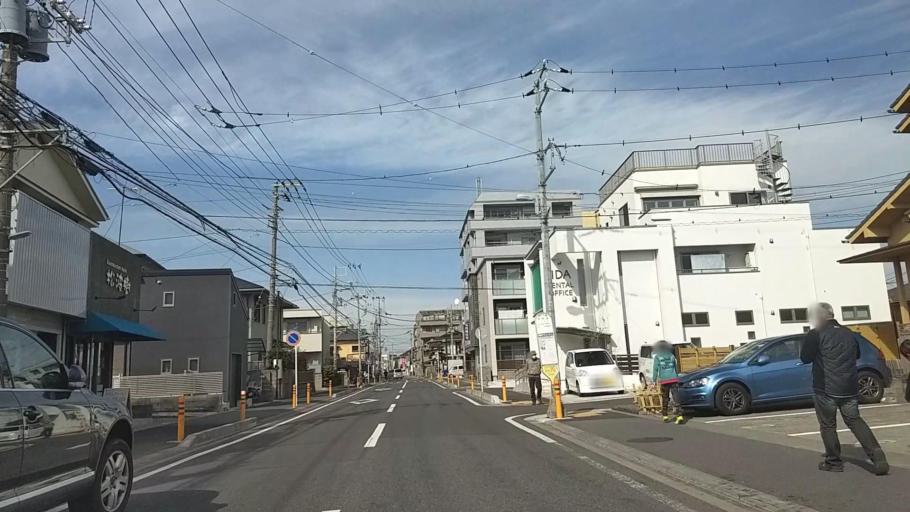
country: JP
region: Kanagawa
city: Chigasaki
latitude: 35.3284
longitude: 139.4380
